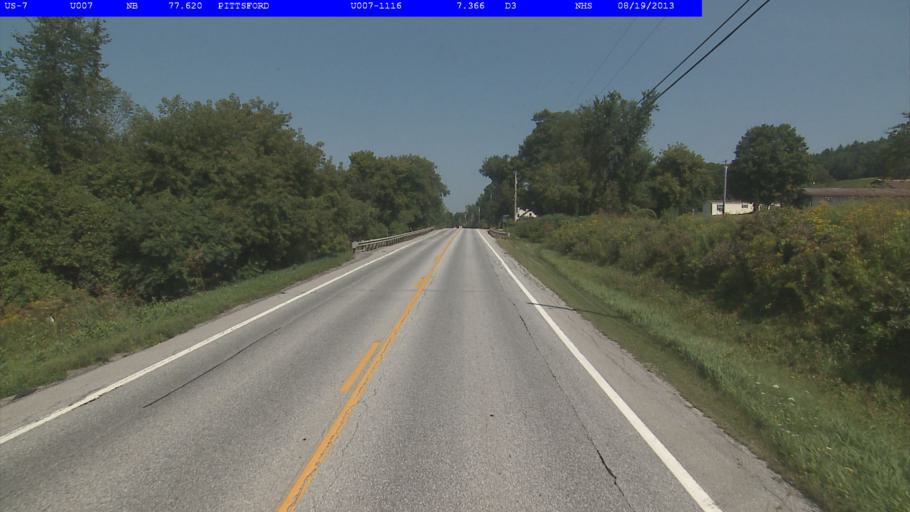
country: US
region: Vermont
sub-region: Rutland County
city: Brandon
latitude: 43.7511
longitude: -73.0478
